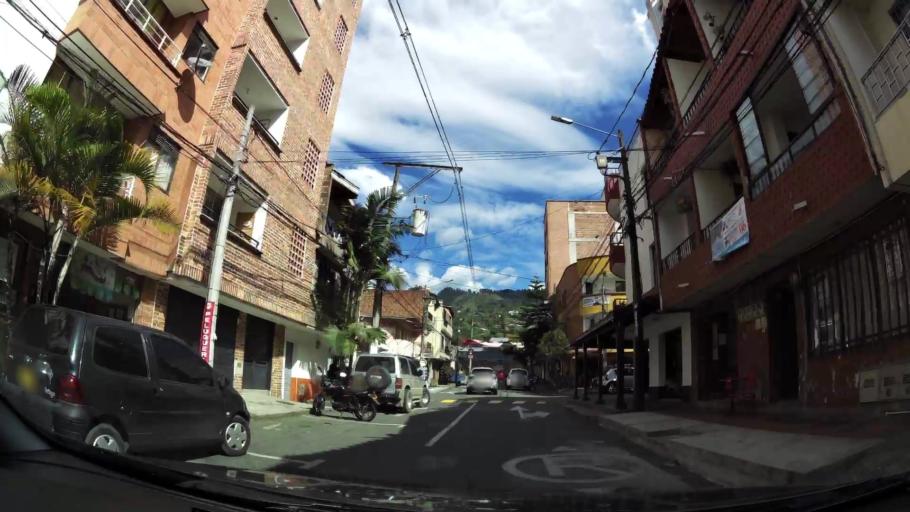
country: CO
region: Antioquia
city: Sabaneta
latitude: 6.1543
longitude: -75.6103
